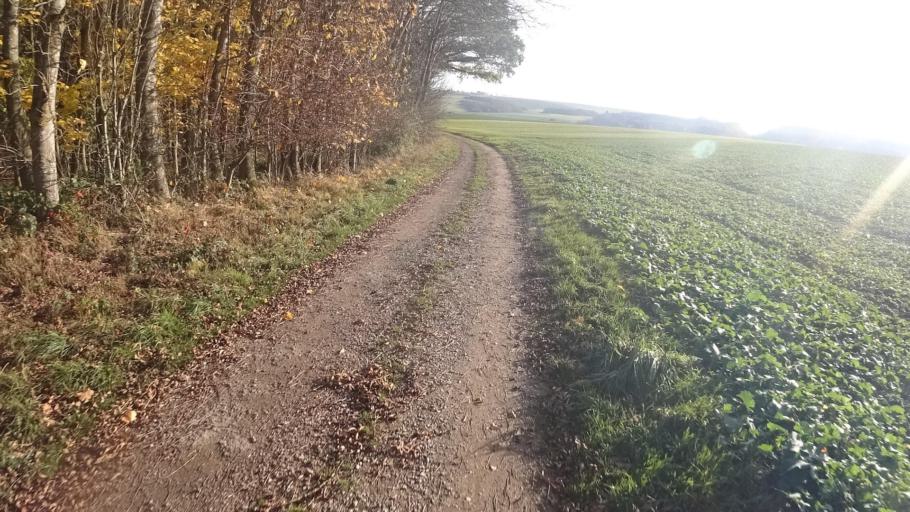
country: DE
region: Rheinland-Pfalz
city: Hausbay
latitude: 50.1112
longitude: 7.5489
